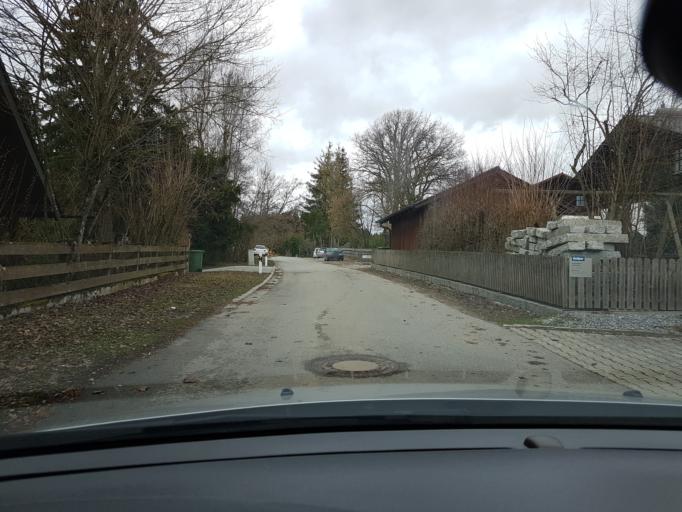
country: DE
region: Bavaria
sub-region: Lower Bavaria
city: Eging
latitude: 48.4937
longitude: 12.1999
